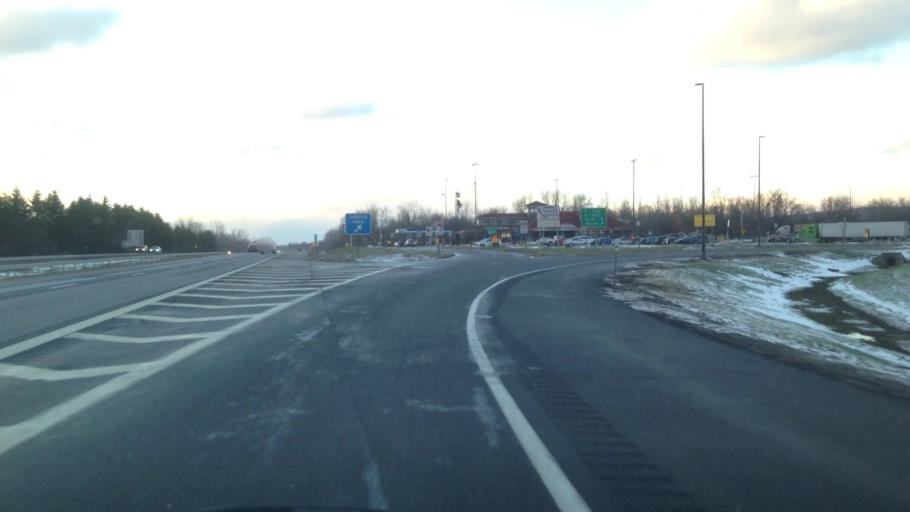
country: US
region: New York
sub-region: Herkimer County
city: Frankfort
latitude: 43.0748
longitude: -75.1014
